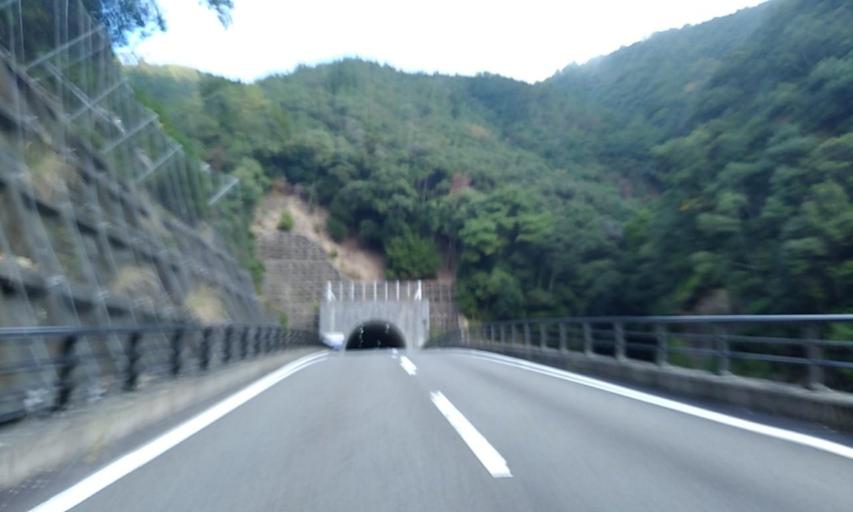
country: JP
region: Wakayama
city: Shingu
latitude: 33.8799
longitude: 135.8769
